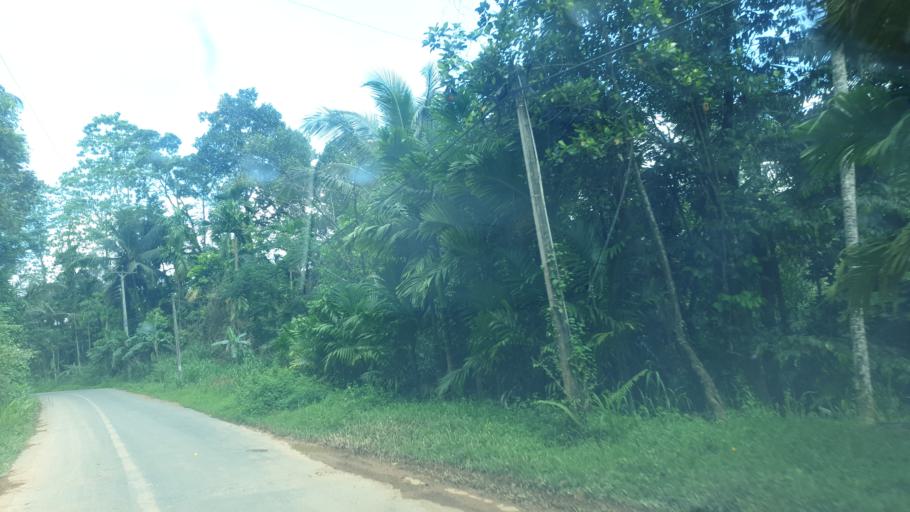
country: LK
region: Sabaragamuwa
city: Ratnapura
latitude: 6.4811
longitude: 80.4131
